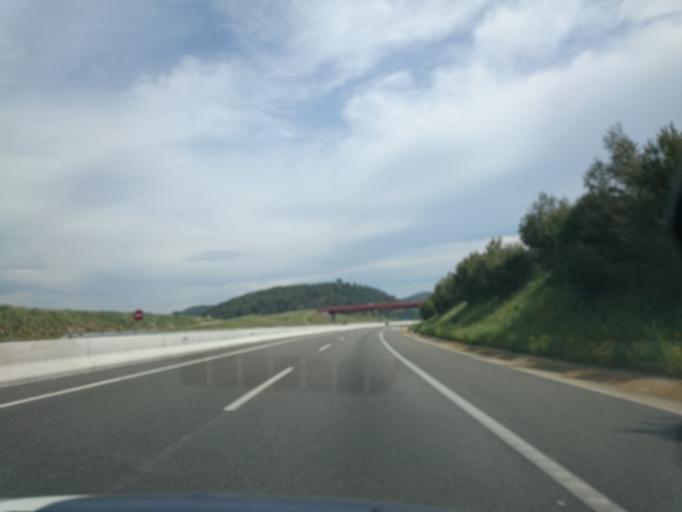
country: ES
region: Catalonia
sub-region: Provincia de Barcelona
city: Avinyo
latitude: 41.8300
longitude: 1.9690
